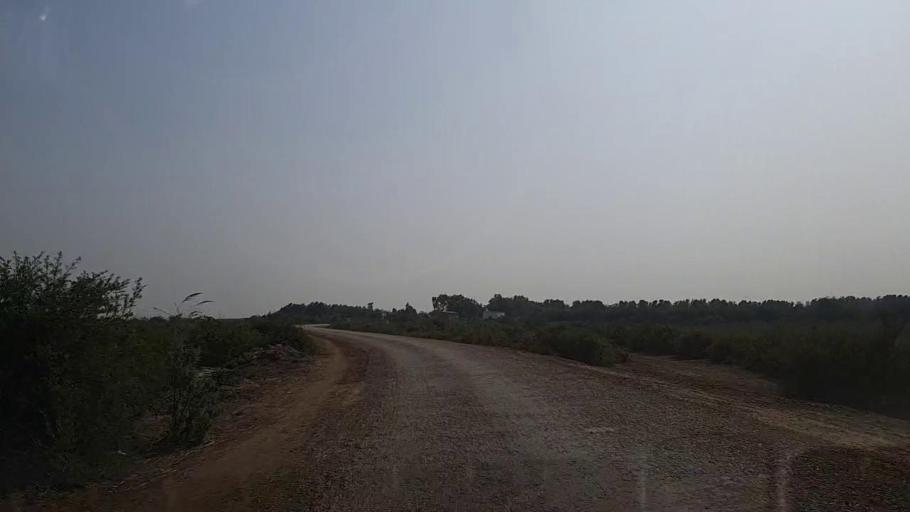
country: PK
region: Sindh
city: Keti Bandar
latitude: 24.2261
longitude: 67.6653
